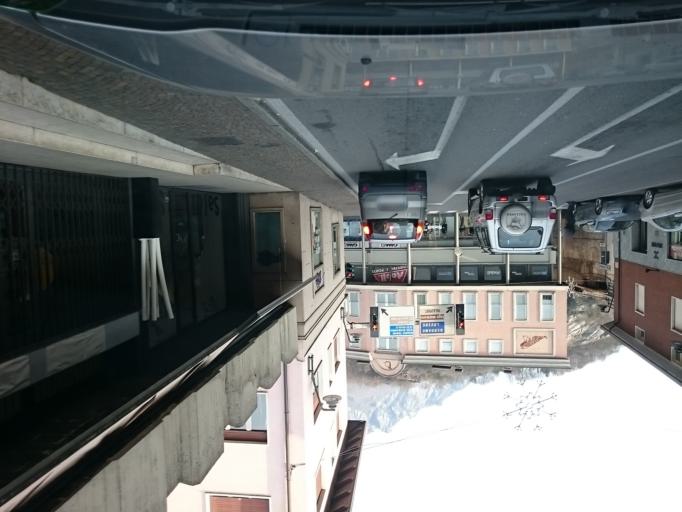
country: IT
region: Lombardy
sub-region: Provincia di Brescia
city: Darfo
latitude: 45.8847
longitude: 10.1807
